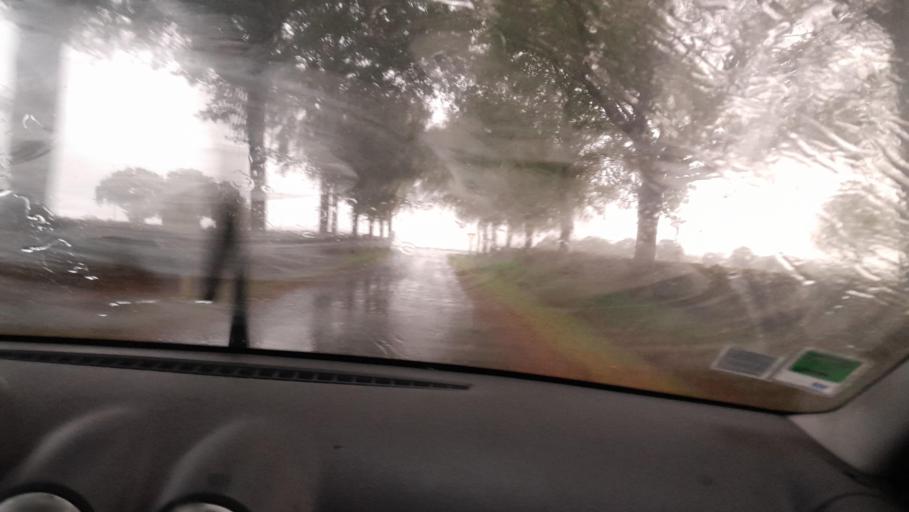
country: FR
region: Pays de la Loire
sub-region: Departement de la Mayenne
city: Ballots
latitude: 47.8611
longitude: -1.0686
